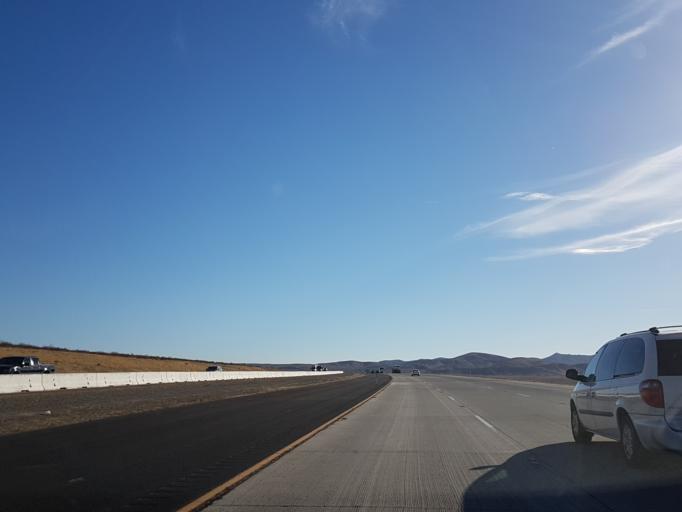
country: US
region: California
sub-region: San Bernardino County
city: Lenwood
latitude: 34.7226
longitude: -117.1941
